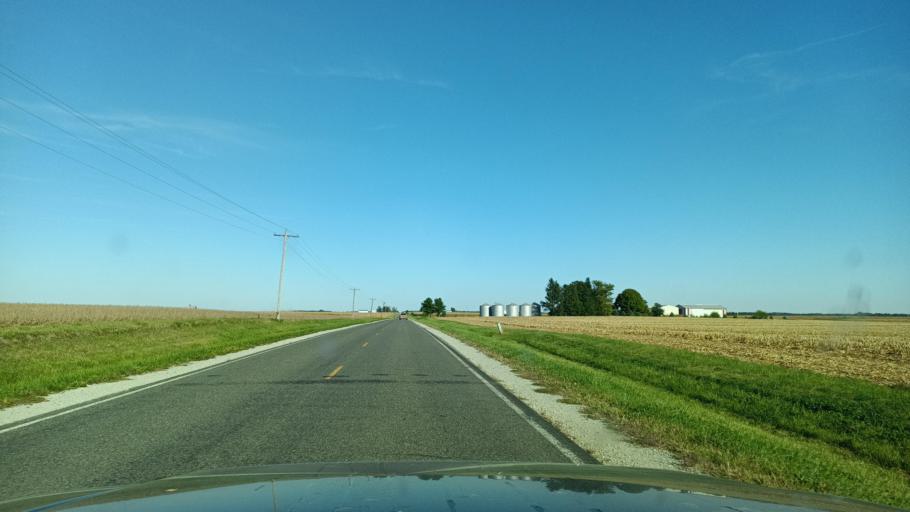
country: US
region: Illinois
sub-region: De Witt County
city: Clinton
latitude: 40.2244
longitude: -88.8936
